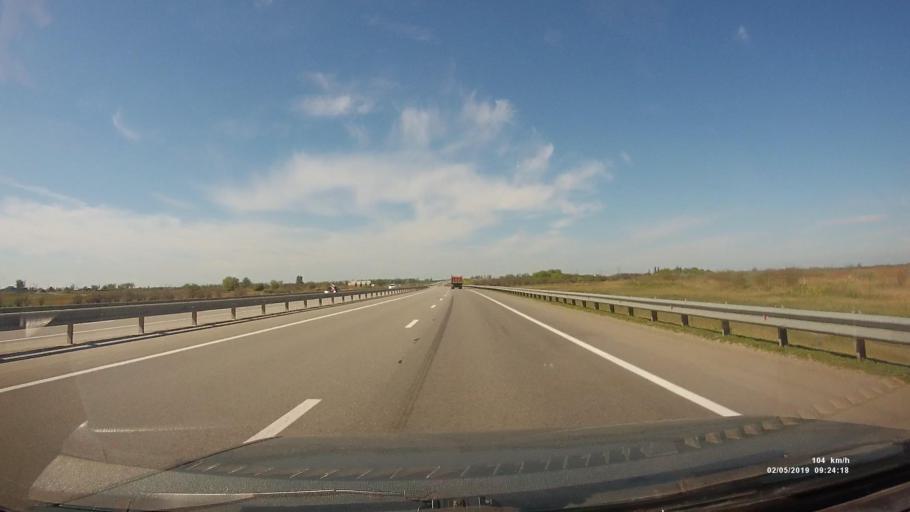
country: RU
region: Rostov
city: Kuleshovka
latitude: 47.1123
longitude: 39.6336
